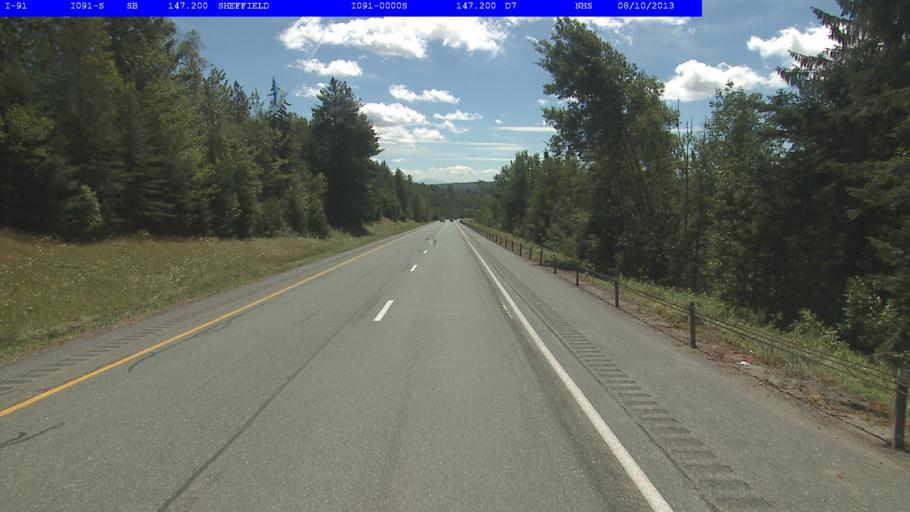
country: US
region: Vermont
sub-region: Caledonia County
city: Lyndonville
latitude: 44.6247
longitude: -72.1271
